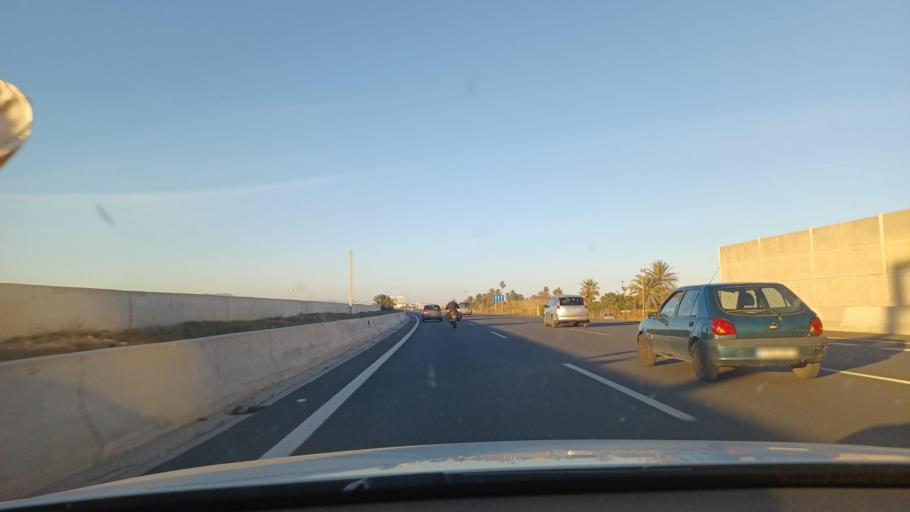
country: ES
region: Valencia
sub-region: Provincia de Valencia
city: Meliana
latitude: 39.5154
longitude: -0.3208
